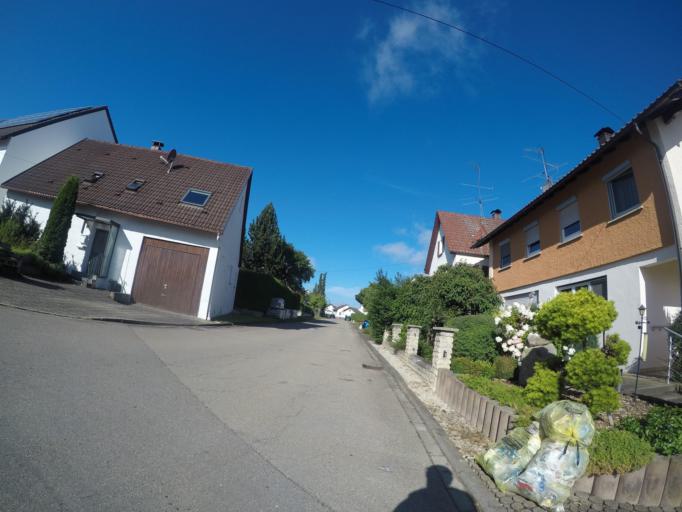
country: DE
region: Baden-Wuerttemberg
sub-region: Tuebingen Region
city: Schelklingen
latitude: 48.3863
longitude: 9.6596
